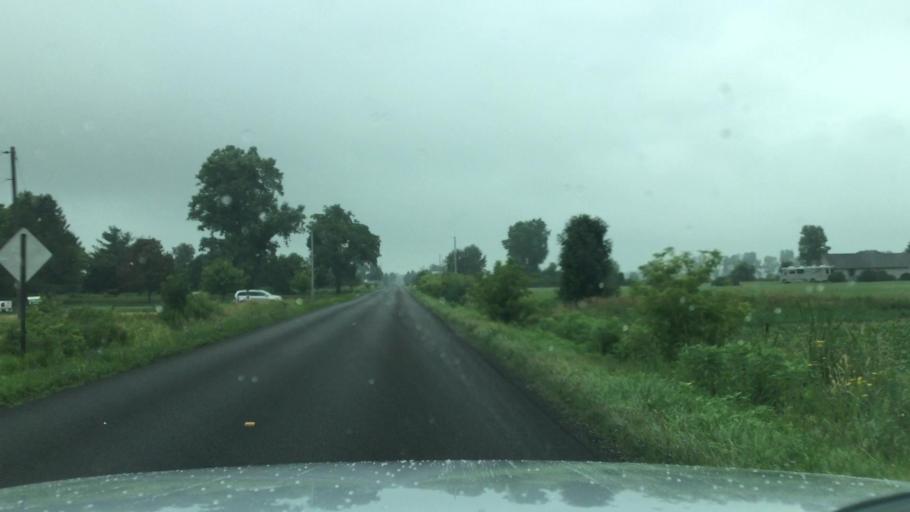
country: US
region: Michigan
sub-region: Shiawassee County
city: New Haven
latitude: 43.0573
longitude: -84.1501
